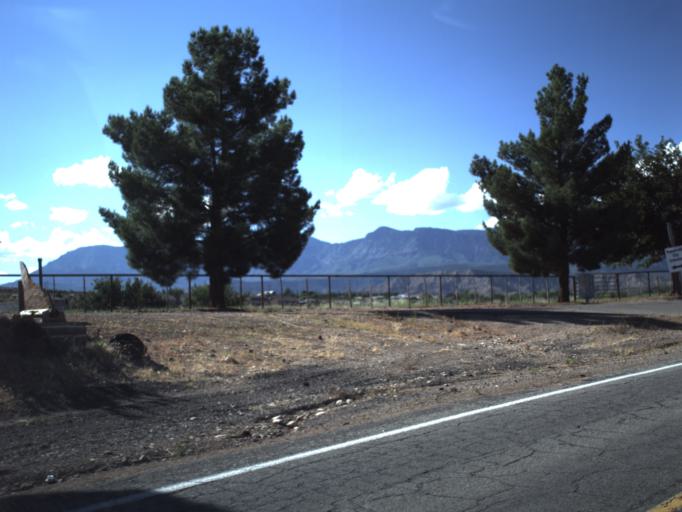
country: US
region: Utah
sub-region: Washington County
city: Toquerville
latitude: 37.2314
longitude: -113.2816
